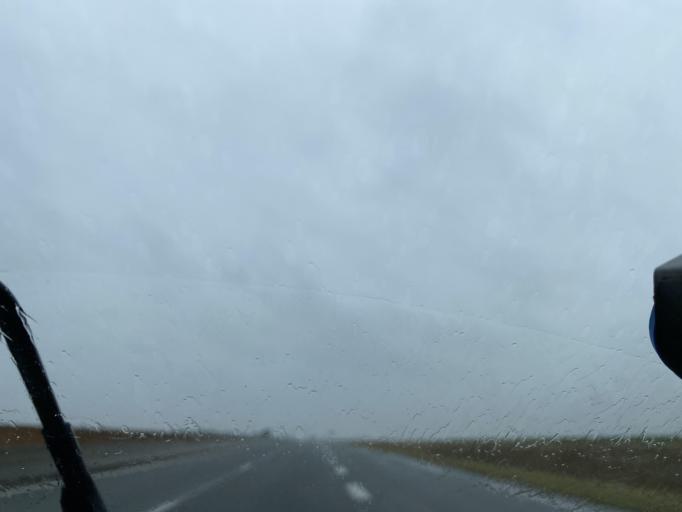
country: FR
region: Centre
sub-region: Departement d'Eure-et-Loir
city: Villemeux-sur-Eure
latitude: 48.6043
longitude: 1.4213
